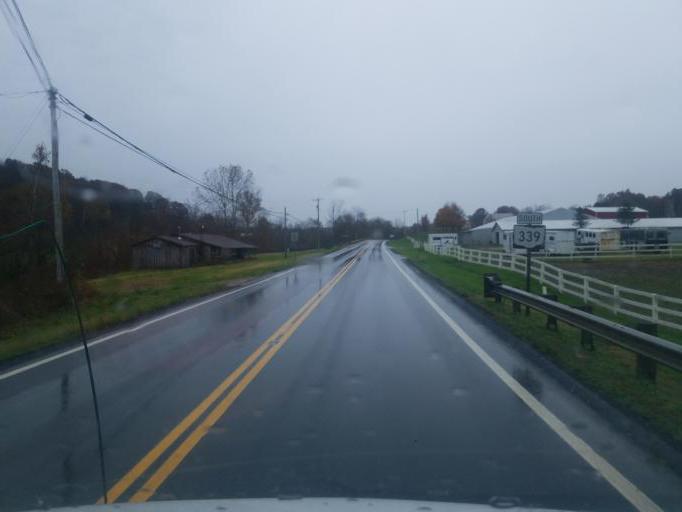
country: US
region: Ohio
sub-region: Washington County
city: Beverly
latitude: 39.4636
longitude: -81.6361
